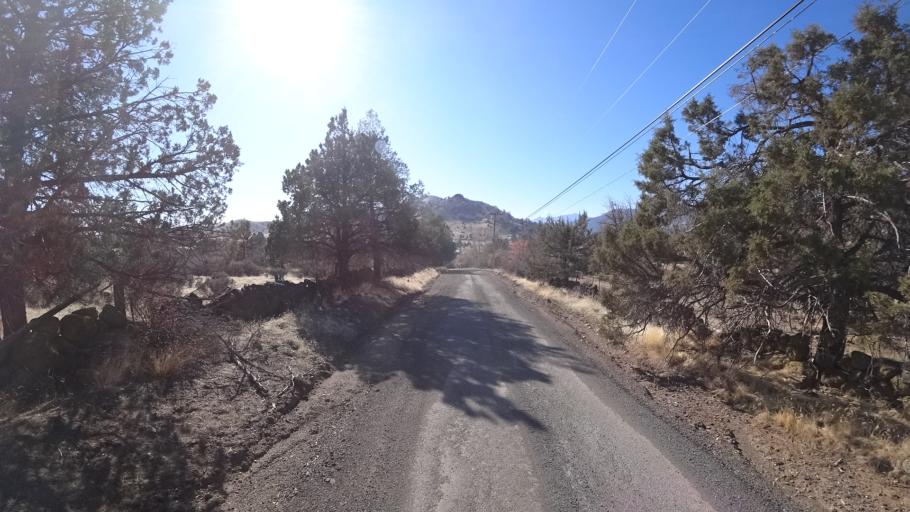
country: US
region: California
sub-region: Siskiyou County
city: Yreka
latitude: 41.7762
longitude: -122.5914
